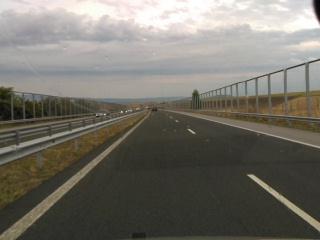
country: BG
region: Sliven
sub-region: Obshtina Sliven
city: Kermen
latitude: 42.5159
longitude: 26.3732
